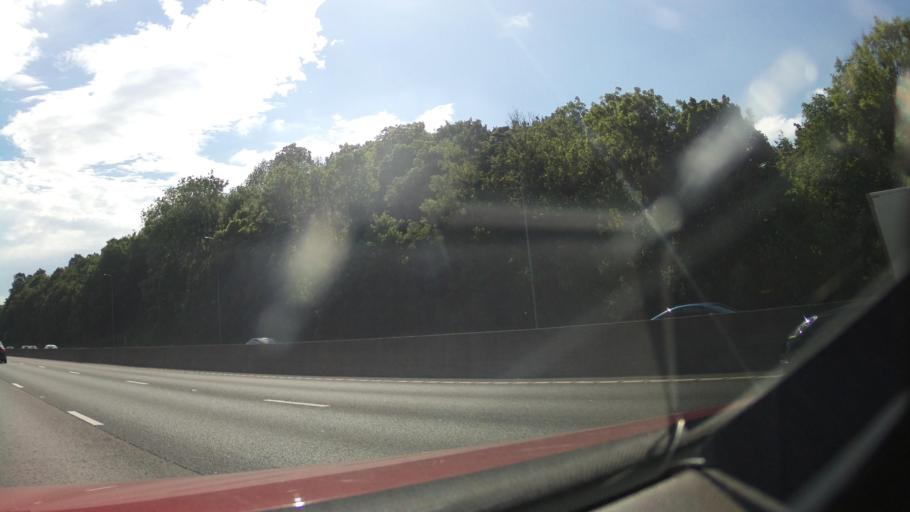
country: GB
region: England
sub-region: City and Borough of Salford
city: Walkden
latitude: 53.5038
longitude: -2.3805
